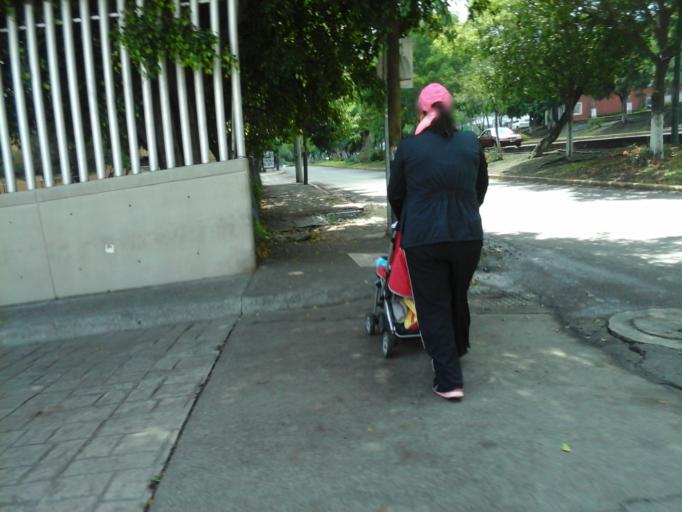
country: MX
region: Michoacan
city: Morelia
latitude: 19.6814
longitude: -101.1841
